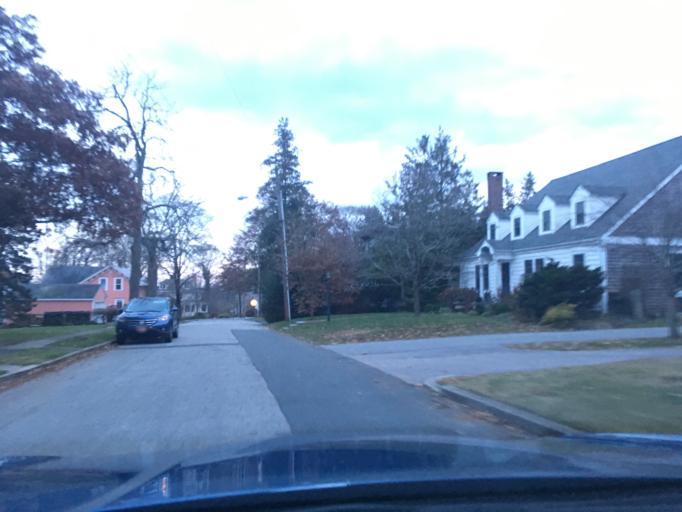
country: US
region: Rhode Island
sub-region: Kent County
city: East Greenwich
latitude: 41.6614
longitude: -71.4550
